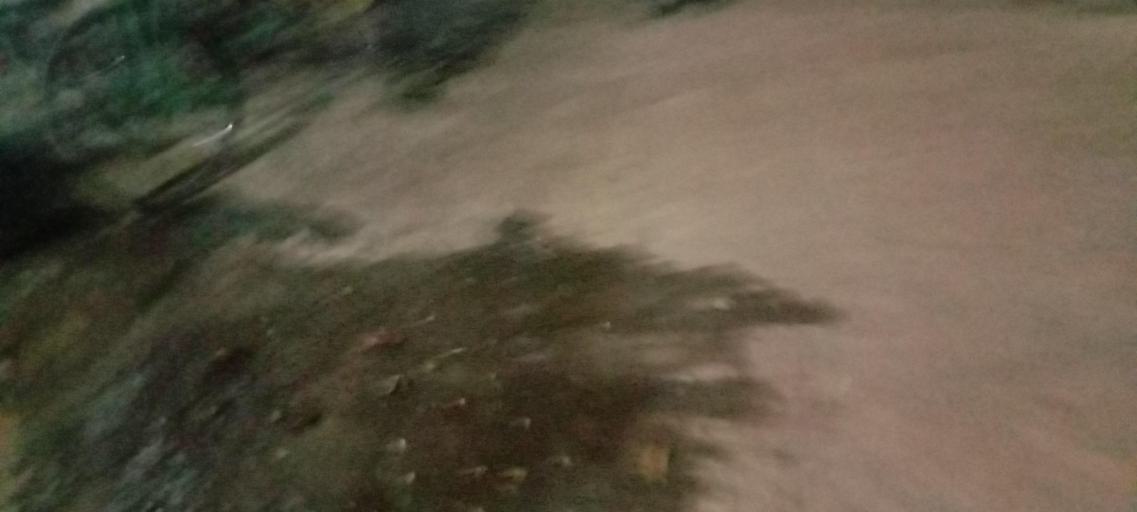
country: BD
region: Dhaka
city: Sakhipur
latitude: 24.4412
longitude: 90.2617
